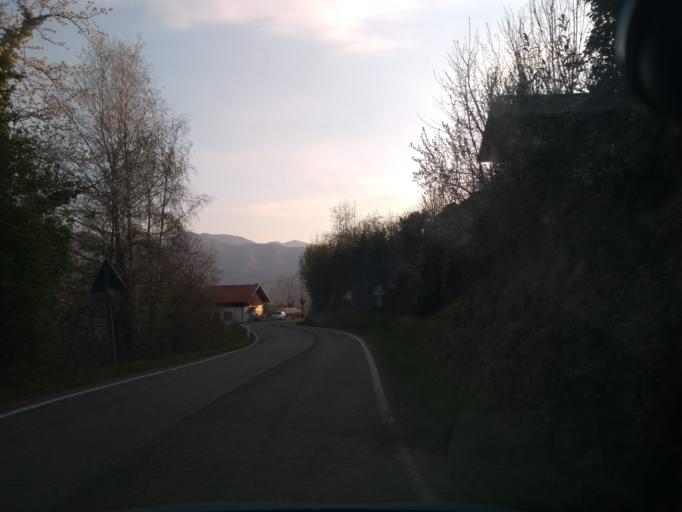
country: IT
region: Piedmont
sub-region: Provincia di Torino
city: Lanzo Torinese
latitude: 45.2919
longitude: 7.4822
